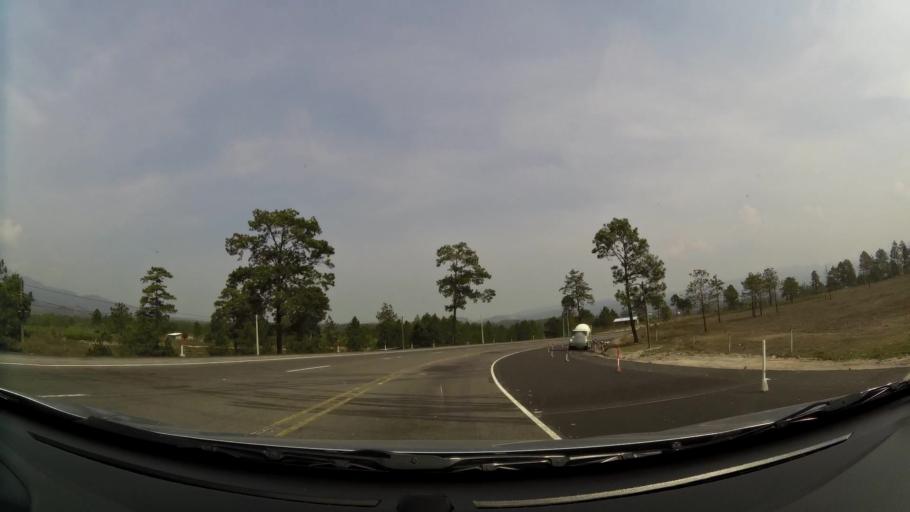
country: HN
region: Comayagua
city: Siguatepeque
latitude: 14.5645
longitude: -87.8296
